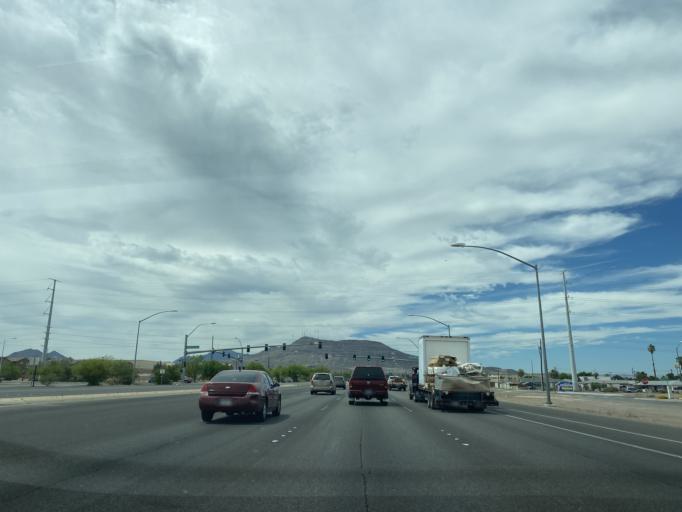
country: US
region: Nevada
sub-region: Clark County
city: Henderson
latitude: 36.0447
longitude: -114.9759
